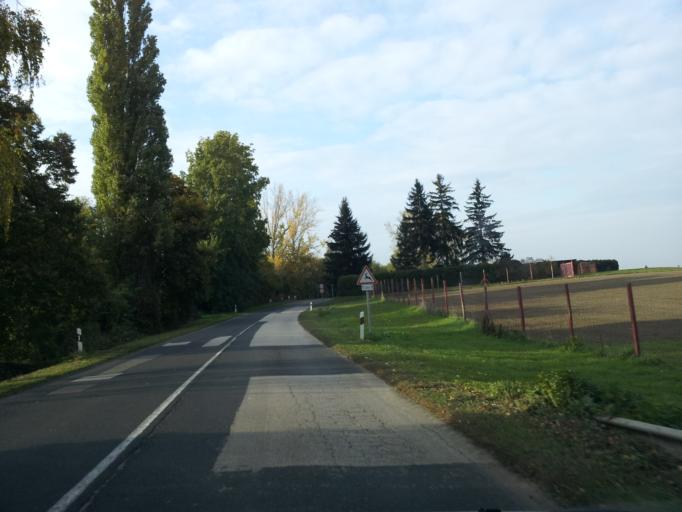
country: HU
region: Gyor-Moson-Sopron
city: Pannonhalma
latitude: 47.5261
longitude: 17.7459
